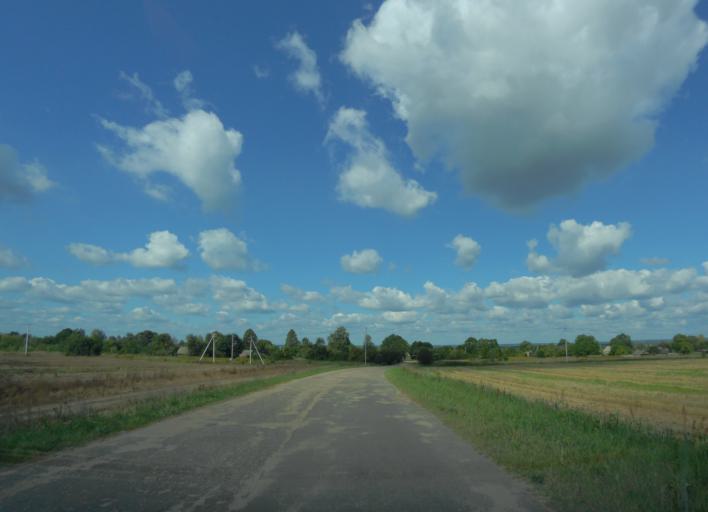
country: BY
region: Minsk
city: Zyembin
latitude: 54.4078
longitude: 28.3893
